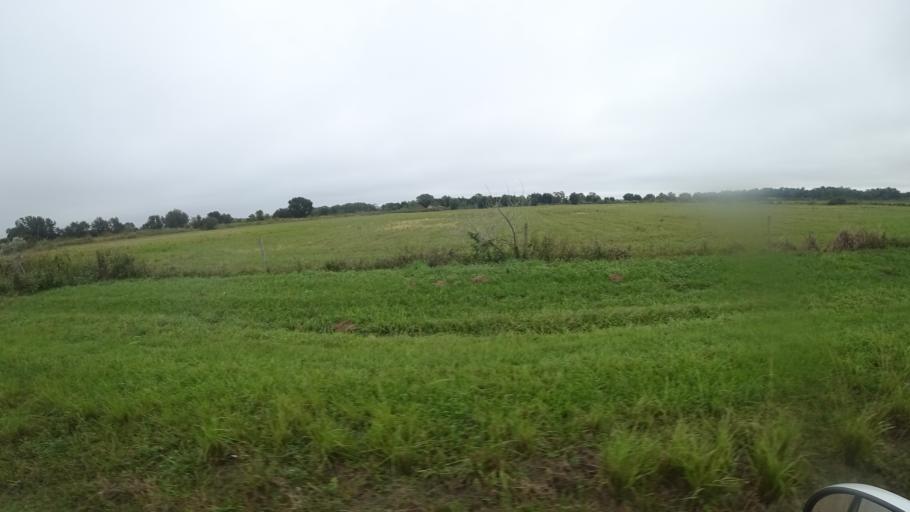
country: US
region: Florida
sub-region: Sarasota County
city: The Meadows
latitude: 27.4460
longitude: -82.3405
